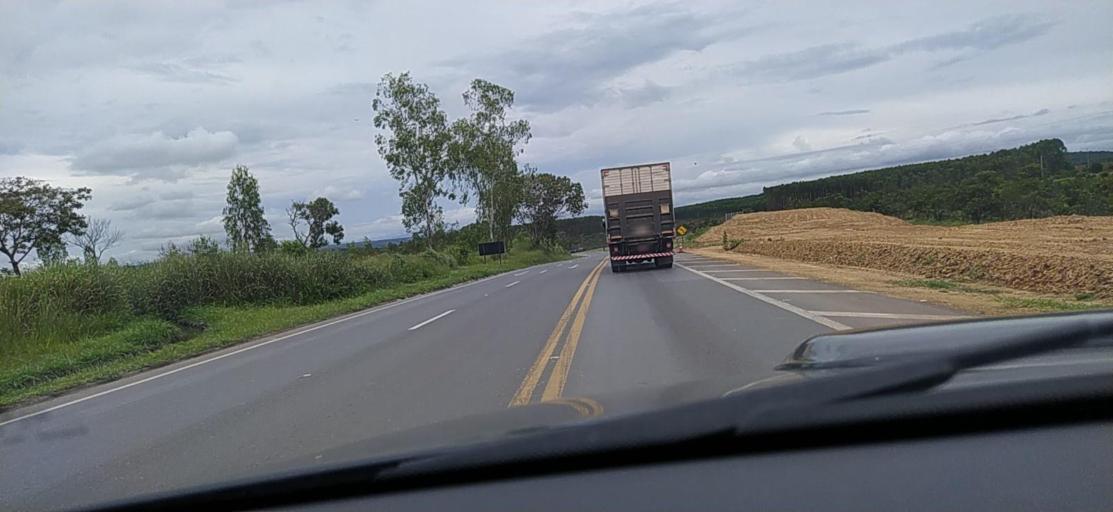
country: BR
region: Minas Gerais
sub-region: Curvelo
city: Curvelo
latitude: -18.7076
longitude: -44.4416
